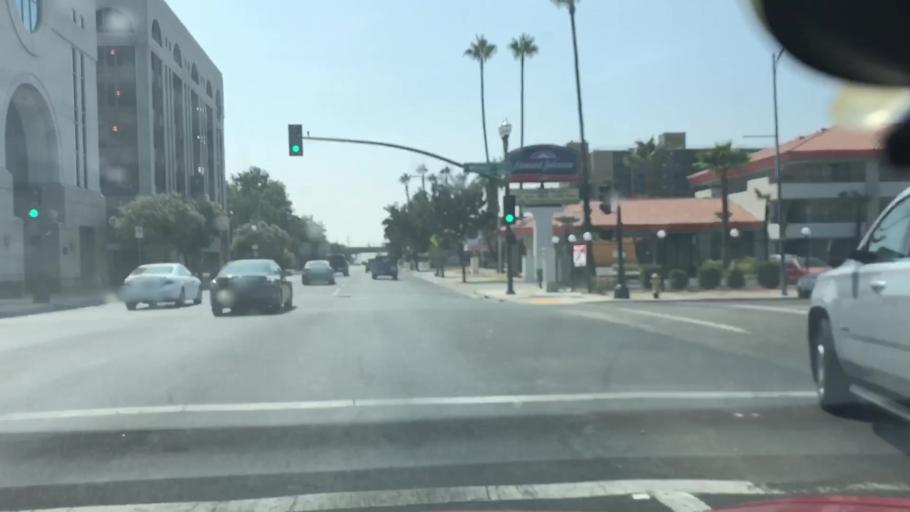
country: US
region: California
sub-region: San Joaquin County
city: Stockton
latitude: 37.9536
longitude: -121.2915
